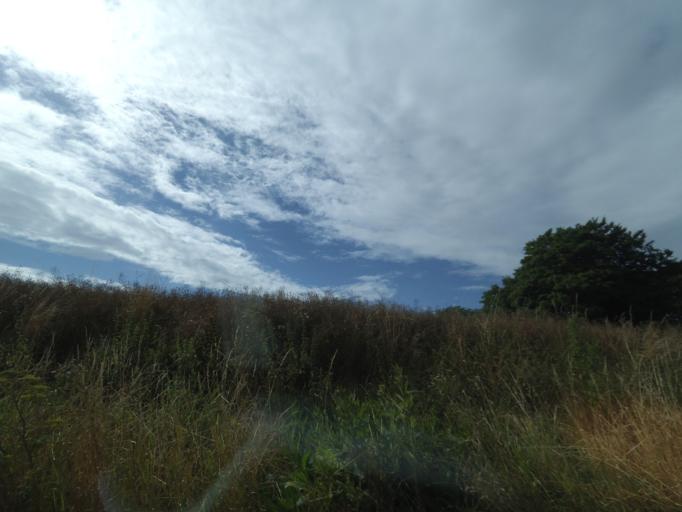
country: DK
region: South Denmark
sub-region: Nordfyns Kommune
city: Sonderso
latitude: 55.4606
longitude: 10.1931
